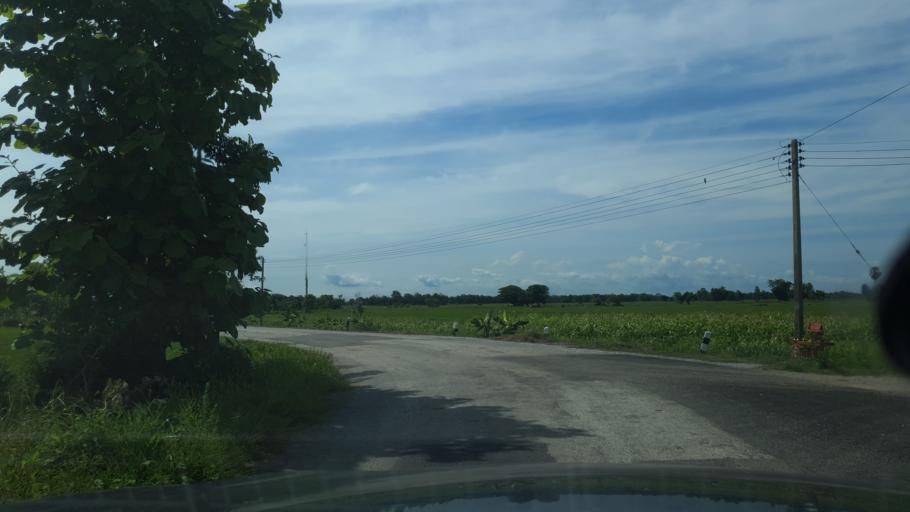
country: TH
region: Sukhothai
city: Si Samrong
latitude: 17.1972
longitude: 99.7259
